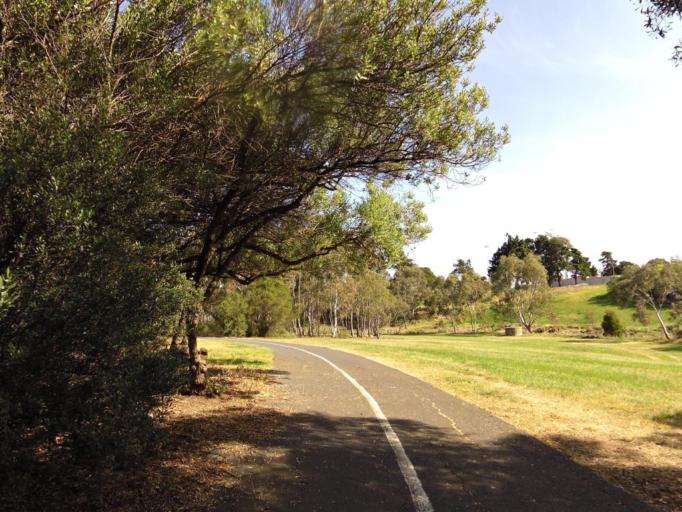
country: AU
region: Victoria
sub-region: Brimbank
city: Sunshine West
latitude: -37.7769
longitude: 144.8074
